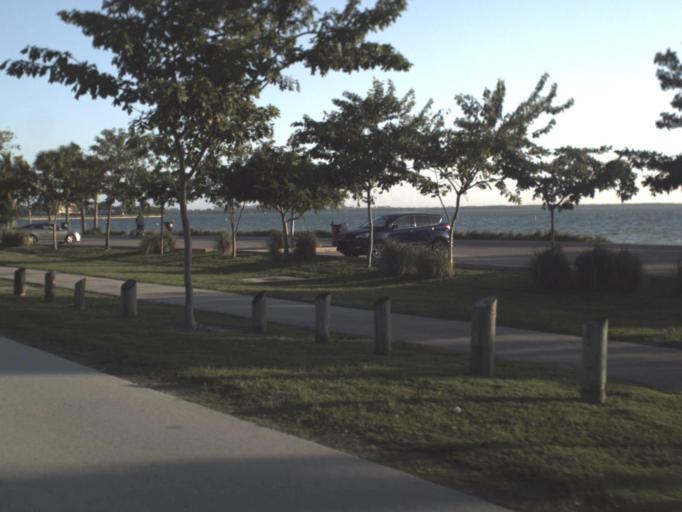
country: US
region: Florida
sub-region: Miami-Dade County
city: Miami
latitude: 25.7405
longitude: -80.1701
